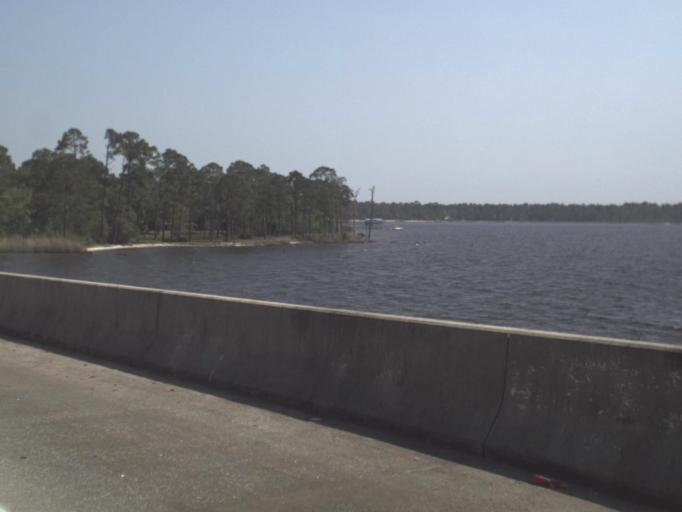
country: US
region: Florida
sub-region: Escambia County
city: Myrtle Grove
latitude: 30.4030
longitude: -87.4275
